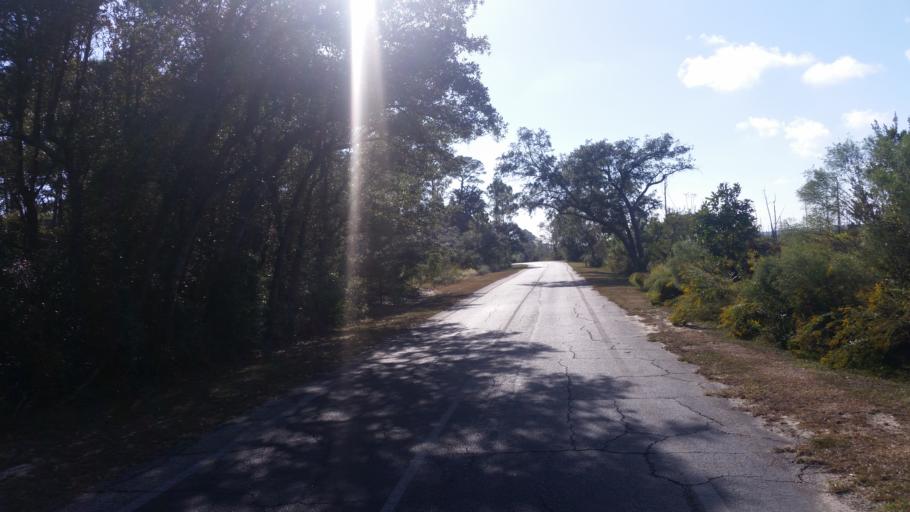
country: US
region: Alabama
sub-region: Baldwin County
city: Orange Beach
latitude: 30.2750
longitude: -87.6171
